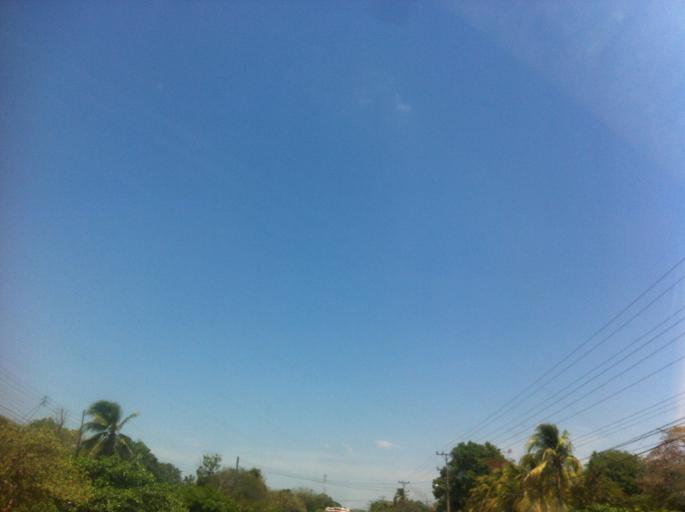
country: CR
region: Guanacaste
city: Sardinal
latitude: 10.4942
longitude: -85.5707
